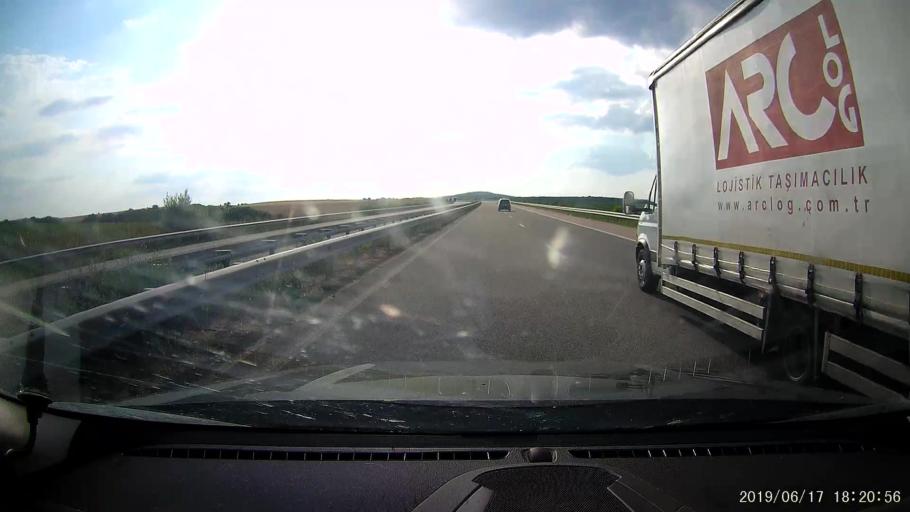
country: BG
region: Khaskovo
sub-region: Obshtina Simeonovgrad
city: Simeonovgrad
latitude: 41.9654
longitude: 25.7984
